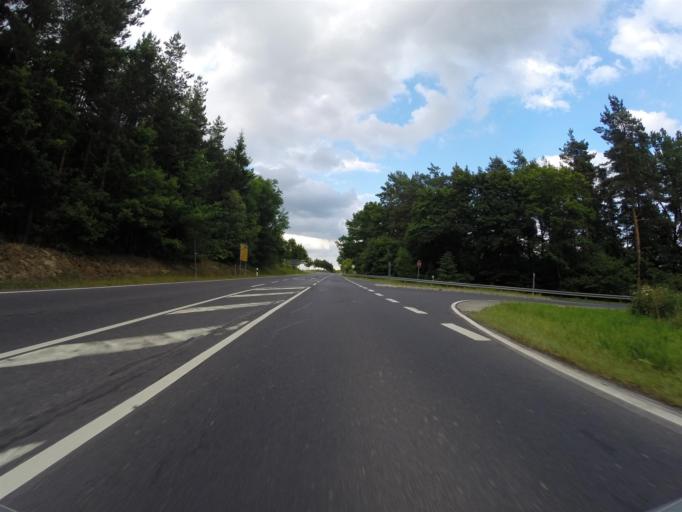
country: DE
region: Thuringia
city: Behringen
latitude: 50.7337
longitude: 11.0130
